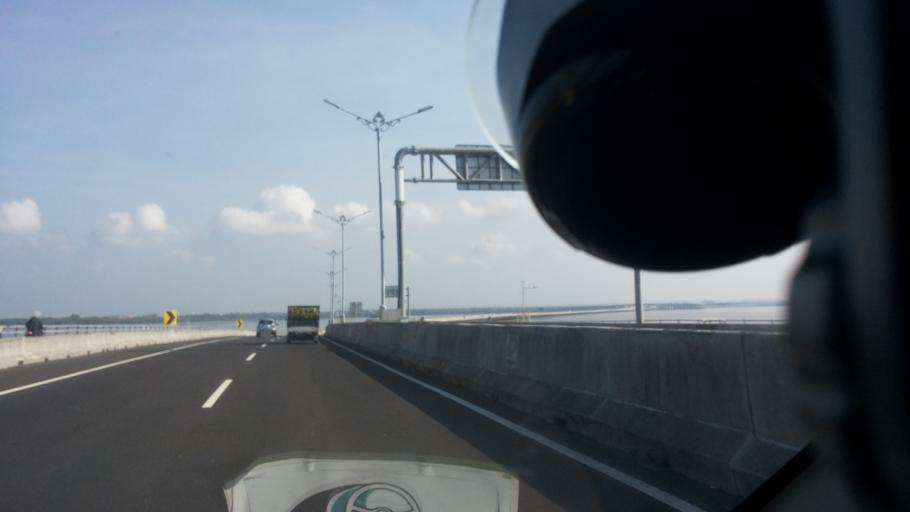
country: ID
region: Bali
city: Kelanabian
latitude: -8.7670
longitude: 115.1974
